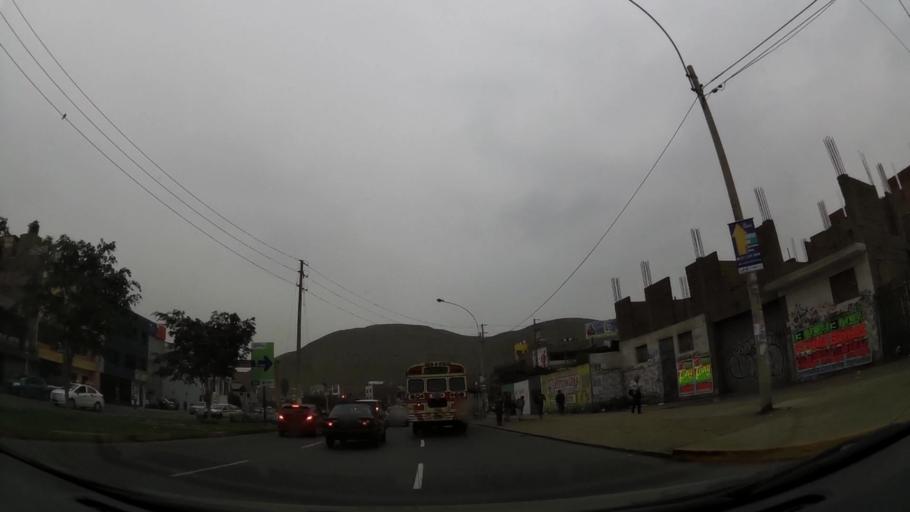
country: PE
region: Lima
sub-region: Lima
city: Independencia
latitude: -11.9387
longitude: -77.0769
